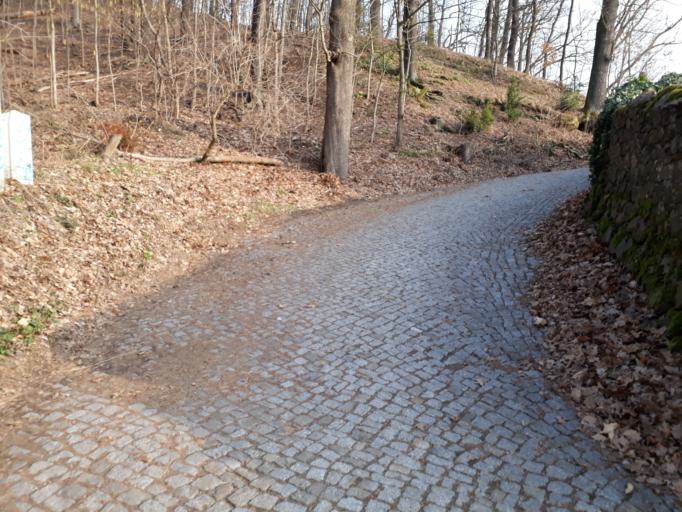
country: DE
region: Saxony
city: Heidenau
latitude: 51.0147
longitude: 13.8714
